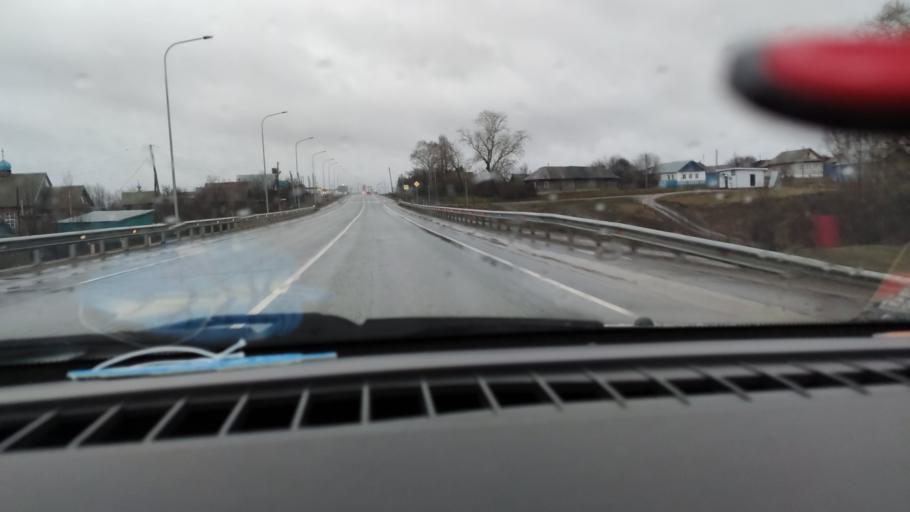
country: RU
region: Tatarstan
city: Mendeleyevsk
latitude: 56.0291
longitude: 52.3736
